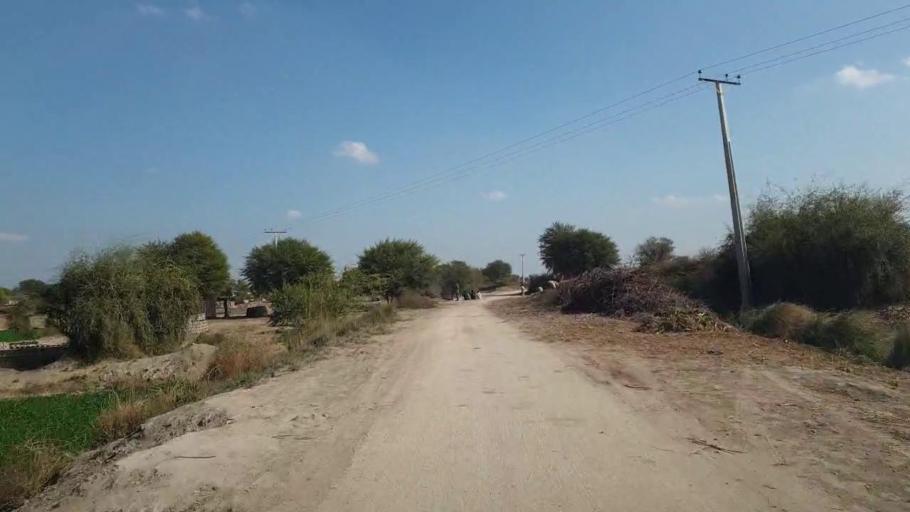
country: PK
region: Sindh
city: Shahpur Chakar
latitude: 26.0883
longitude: 68.5791
